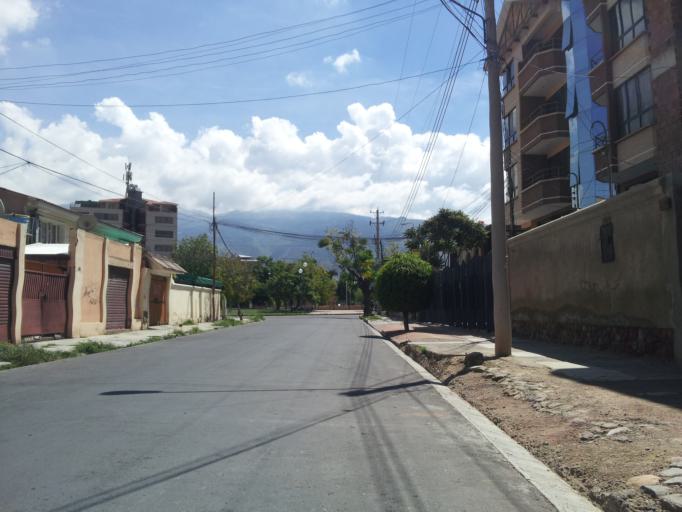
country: BO
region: Cochabamba
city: Cochabamba
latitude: -17.3861
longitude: -66.1738
